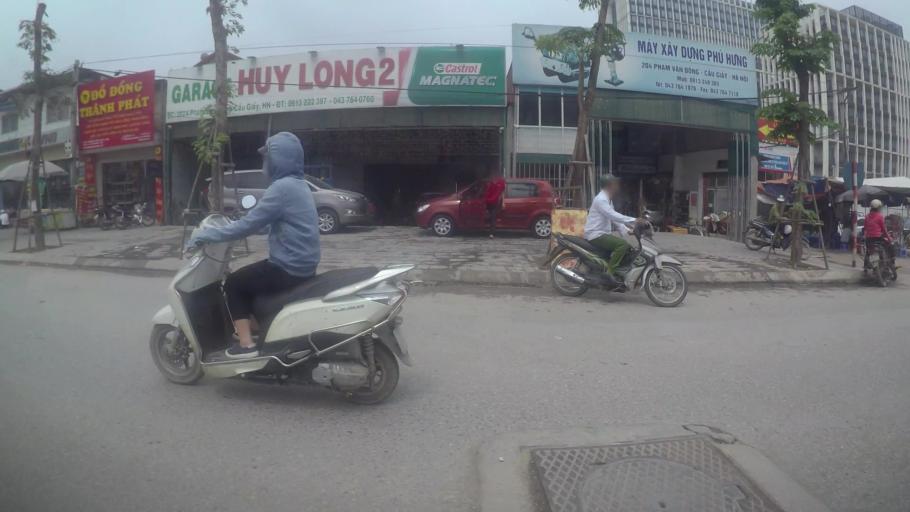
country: VN
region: Ha Noi
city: Cau Dien
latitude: 21.0470
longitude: 105.7813
